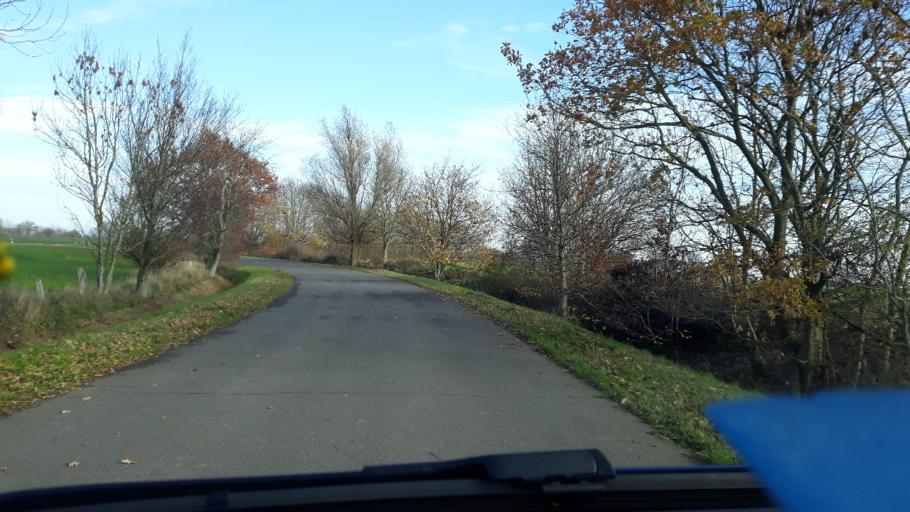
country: DE
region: Schleswig-Holstein
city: Brodersby
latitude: 54.6479
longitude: 10.0116
